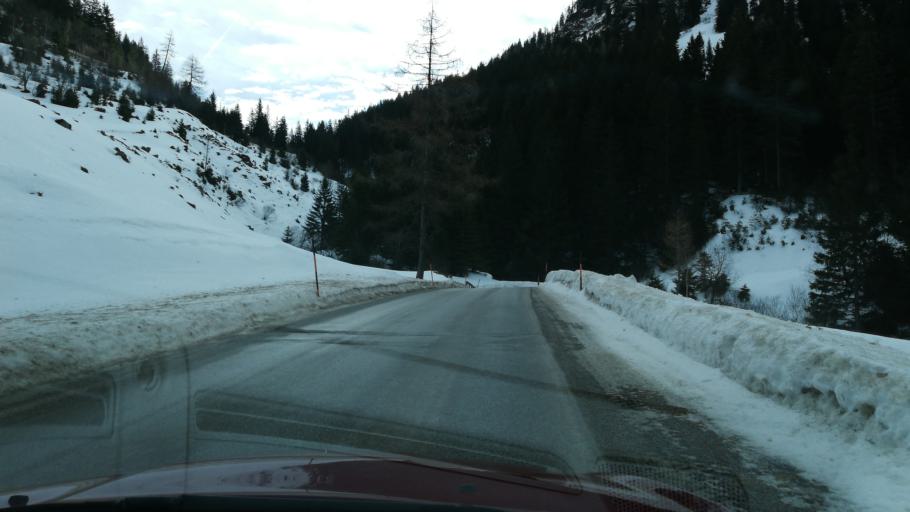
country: AT
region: Styria
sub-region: Politischer Bezirk Liezen
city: Donnersbach
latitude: 47.4115
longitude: 14.1808
